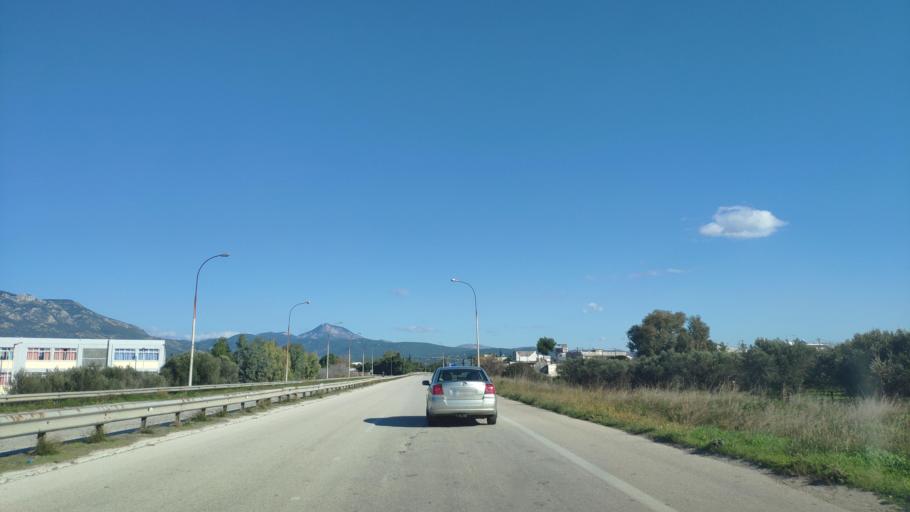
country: GR
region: Peloponnese
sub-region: Nomos Korinthias
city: Korinthos
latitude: 37.9355
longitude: 22.9492
